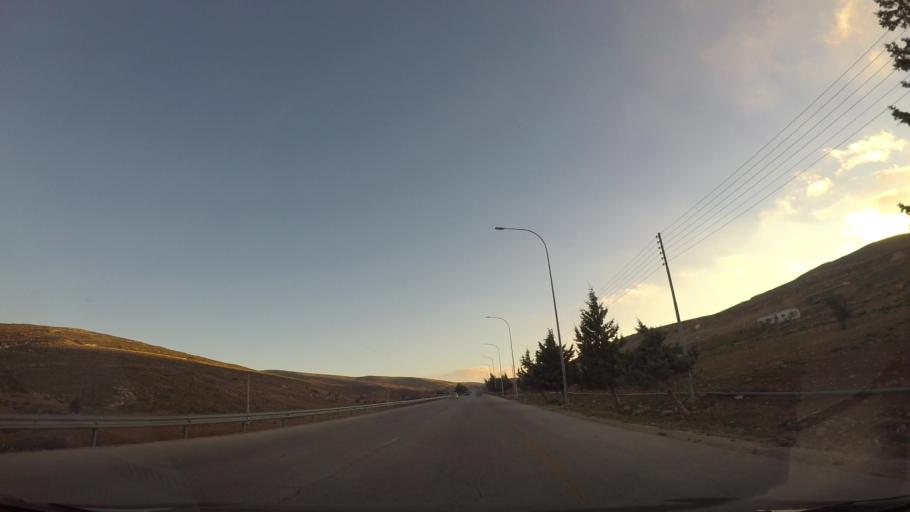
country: JO
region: Ma'an
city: Petra
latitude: 30.4289
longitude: 35.5148
